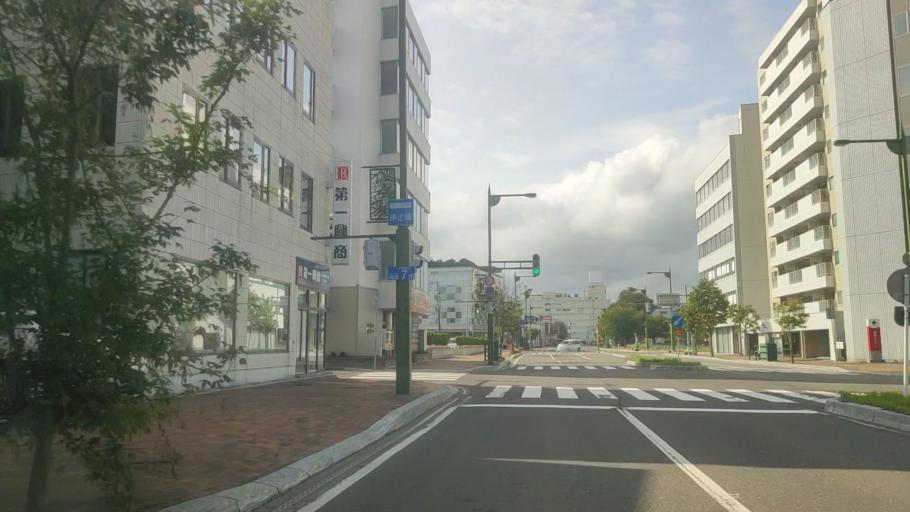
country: JP
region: Hokkaido
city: Tomakomai
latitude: 42.6346
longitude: 141.6012
